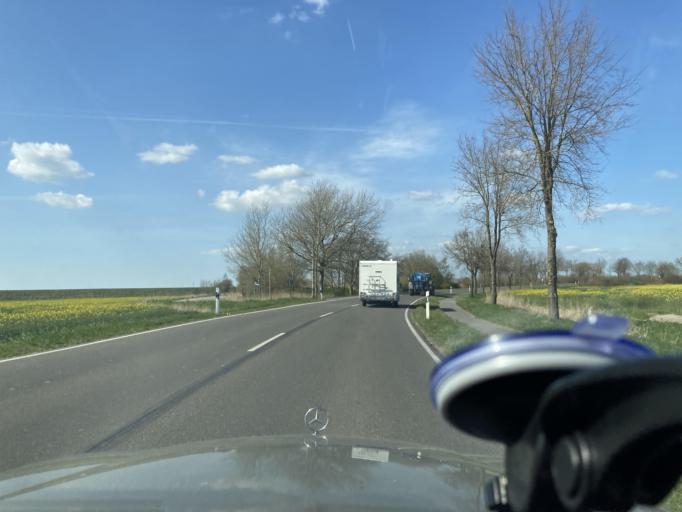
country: DE
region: Schleswig-Holstein
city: Friedrichstadt
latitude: 54.3632
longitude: 9.0906
